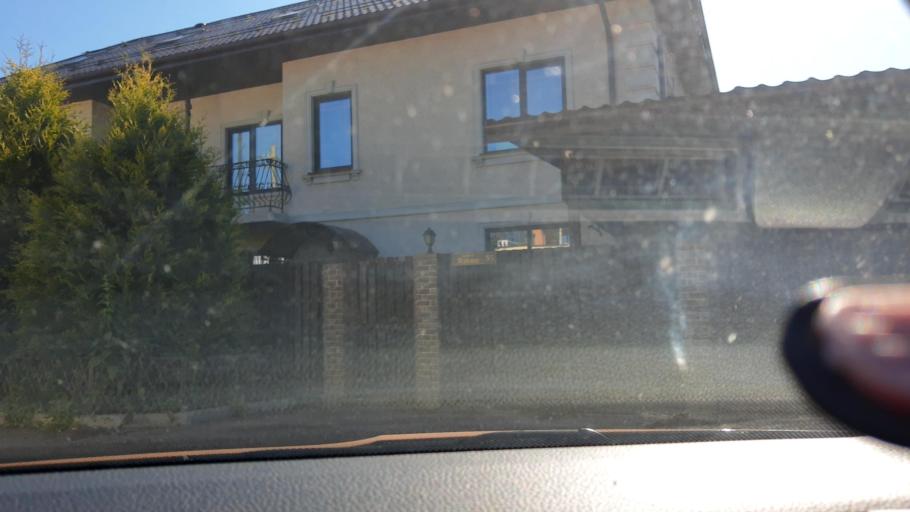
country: RU
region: Moskovskaya
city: Kommunarka
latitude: 55.5229
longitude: 37.5002
